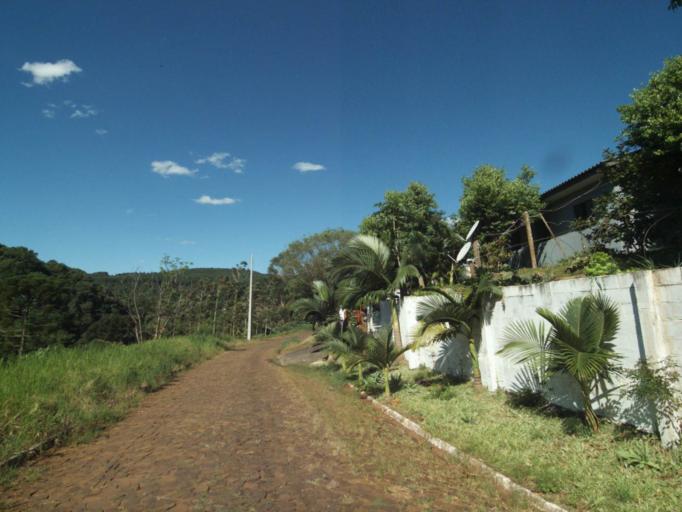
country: BR
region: Parana
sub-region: Ampere
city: Ampere
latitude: -26.1691
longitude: -53.3678
